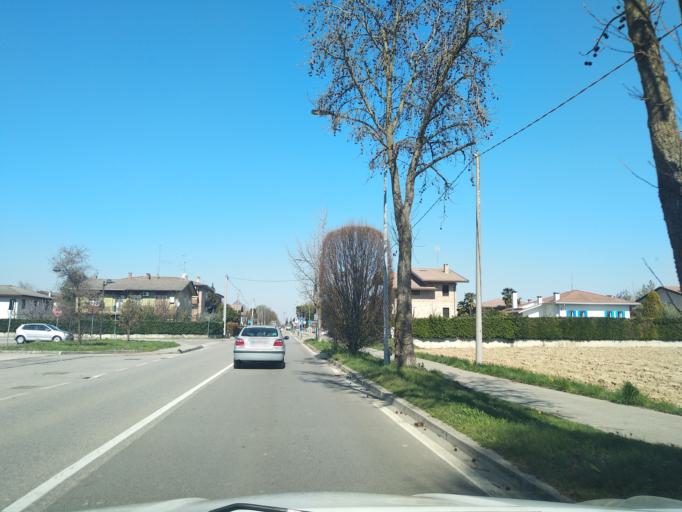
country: IT
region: Veneto
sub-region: Provincia di Padova
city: Bosco
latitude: 45.4408
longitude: 11.7941
